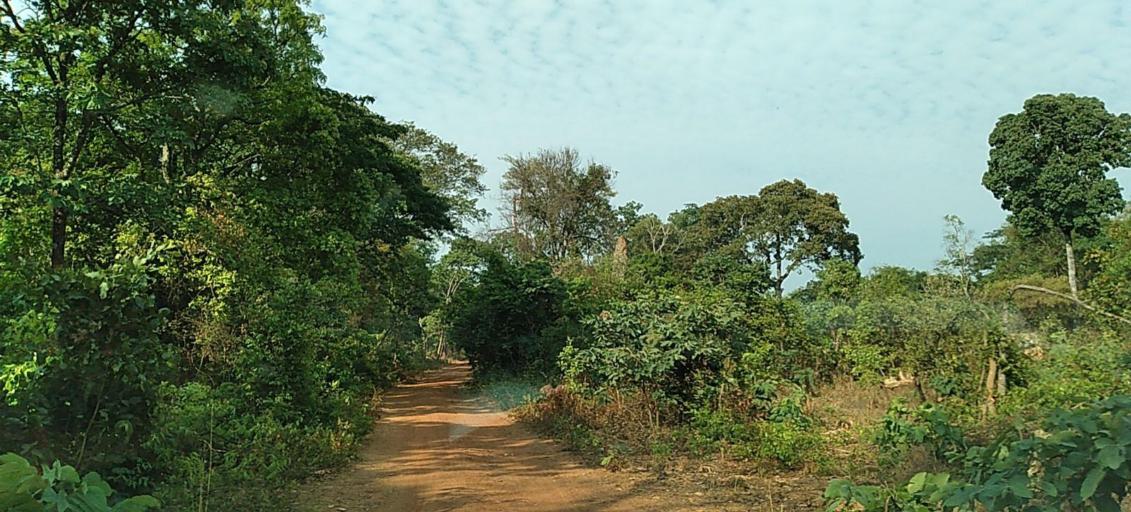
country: ZM
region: Copperbelt
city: Kalulushi
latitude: -12.9893
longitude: 27.7180
